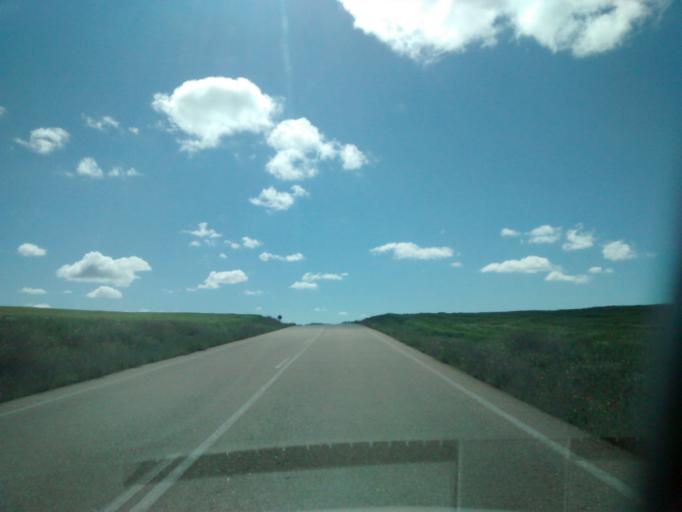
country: ES
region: Aragon
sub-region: Provincia de Zaragoza
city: Perdiguera
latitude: 41.8002
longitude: -0.6776
